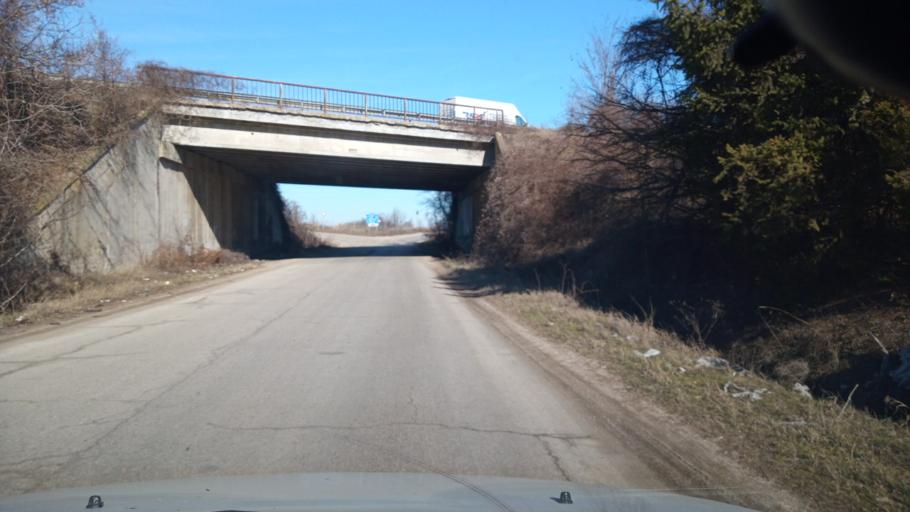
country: BG
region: Pleven
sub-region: Obshtina Pleven
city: Pleven
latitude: 43.4256
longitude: 24.7068
